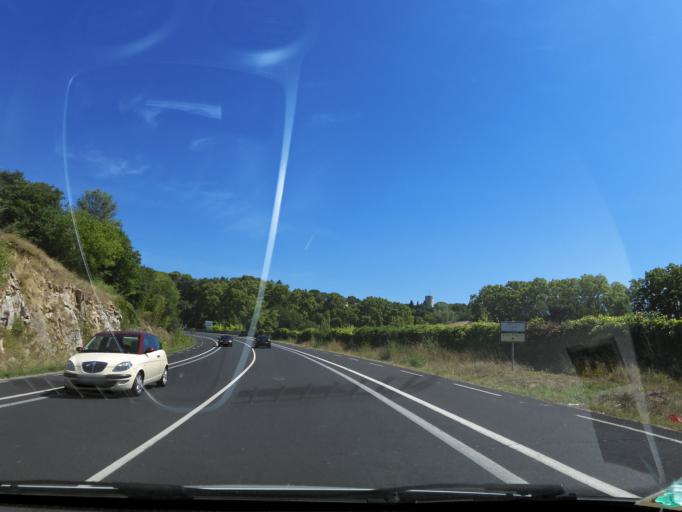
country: FR
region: Languedoc-Roussillon
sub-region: Departement de l'Herault
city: Castelnau-le-Lez
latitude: 43.6442
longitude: 3.8916
